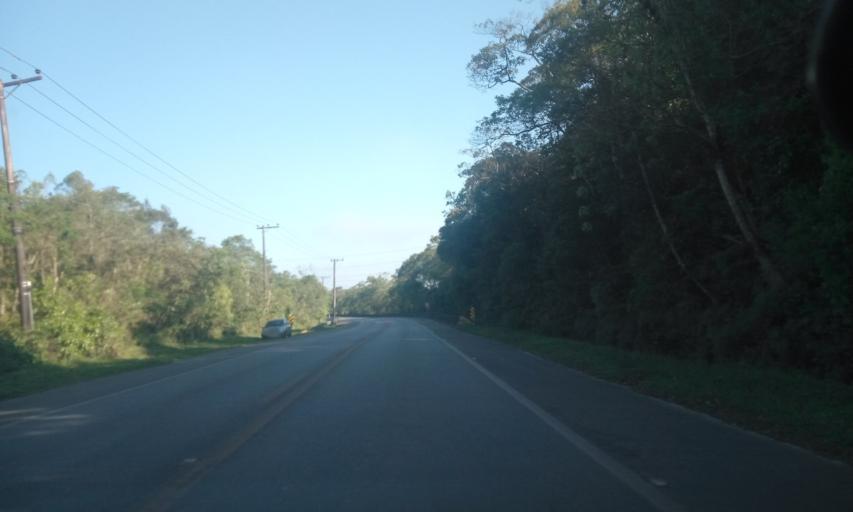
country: BR
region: Sao Paulo
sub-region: Cubatao
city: Cubatao
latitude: -23.8242
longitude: -46.4763
